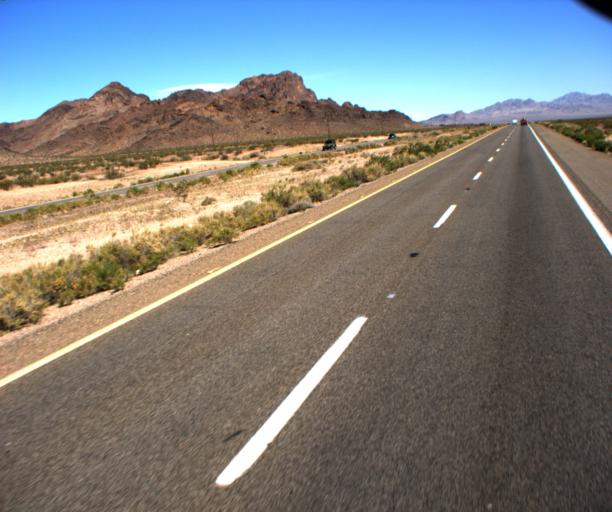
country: US
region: Arizona
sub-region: Mohave County
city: Dolan Springs
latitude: 35.7705
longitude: -114.5125
